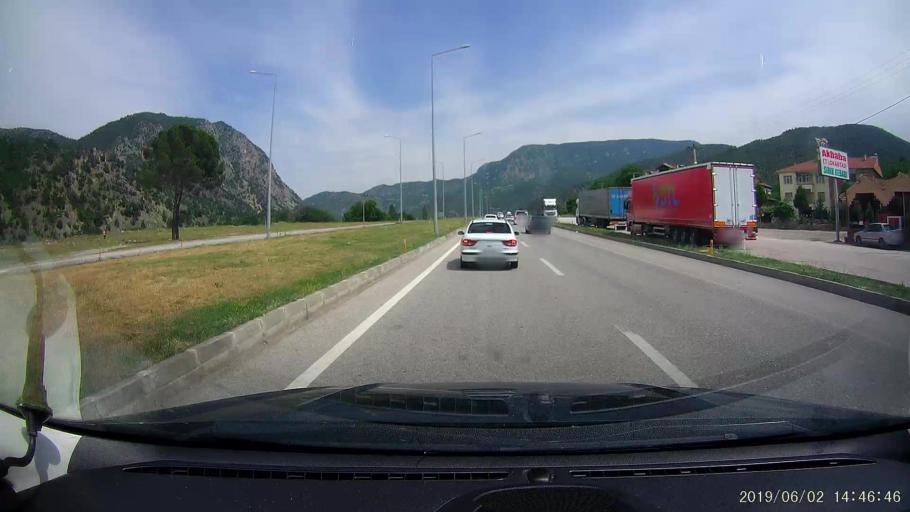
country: TR
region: Corum
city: Hacihamza
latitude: 41.0742
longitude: 34.4542
